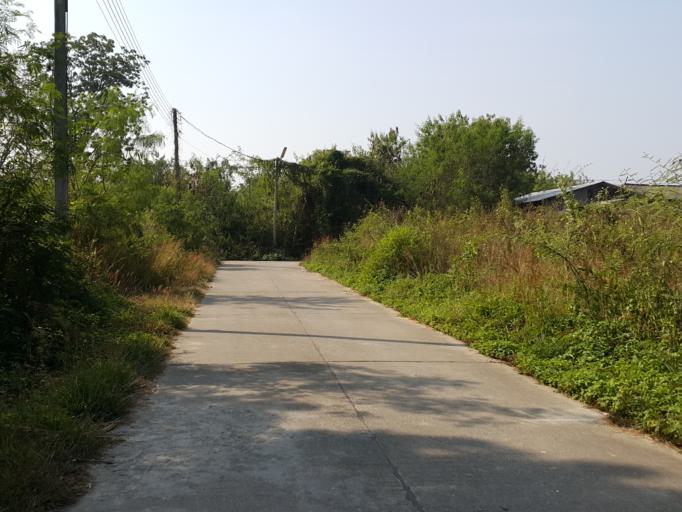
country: TH
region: Chiang Mai
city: San Kamphaeng
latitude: 18.7659
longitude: 99.0872
